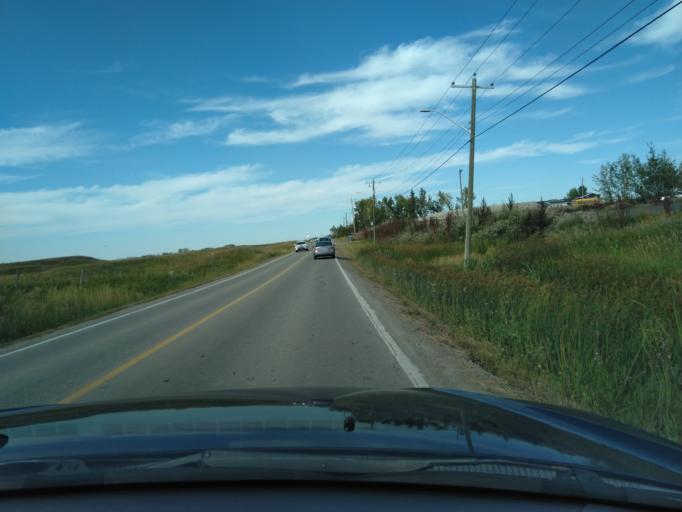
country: CA
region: Alberta
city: Calgary
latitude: 51.1158
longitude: -113.9817
